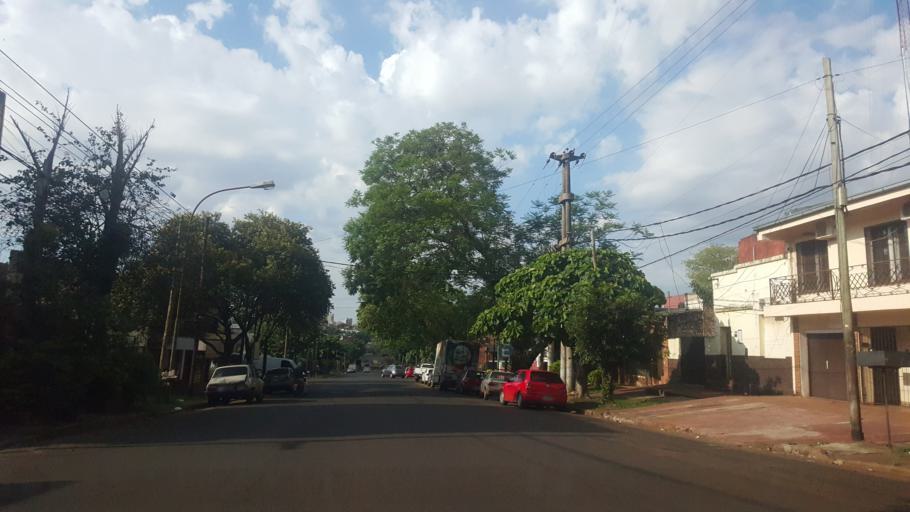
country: AR
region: Misiones
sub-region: Departamento de Capital
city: Posadas
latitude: -27.3845
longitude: -55.8961
